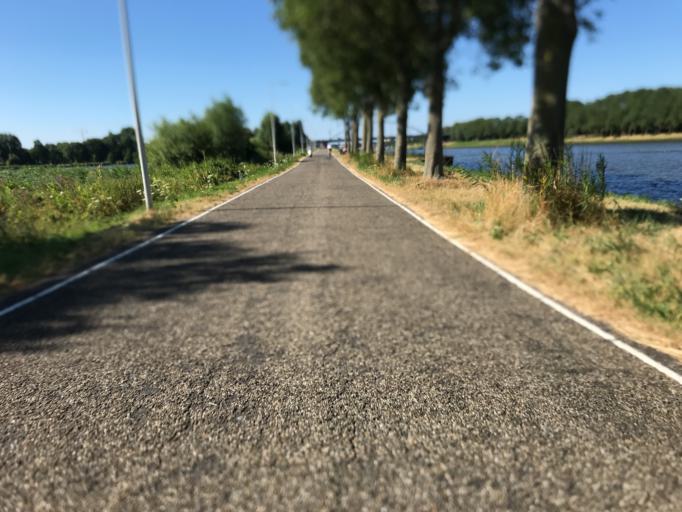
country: NL
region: North Holland
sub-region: Gemeente Diemen
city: Diemen
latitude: 52.3611
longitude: 4.9577
